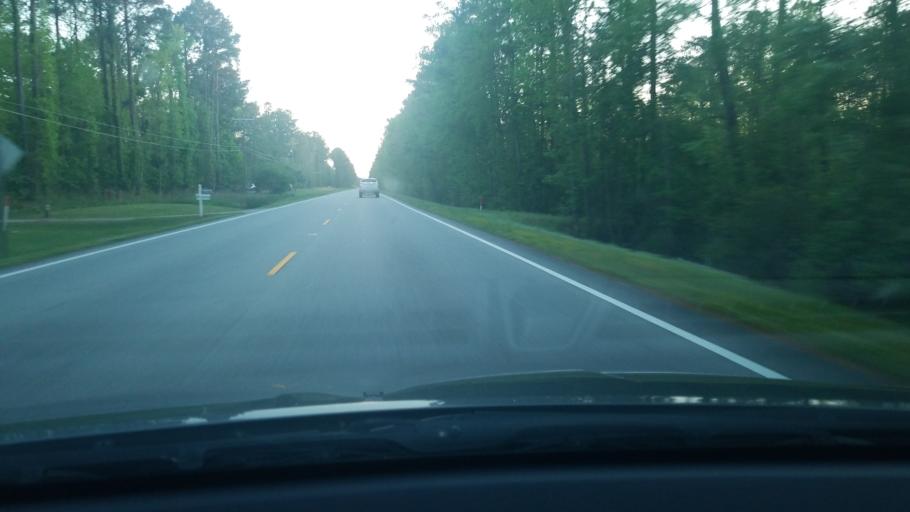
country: US
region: North Carolina
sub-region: Craven County
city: Vanceboro
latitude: 35.2466
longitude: -77.0924
